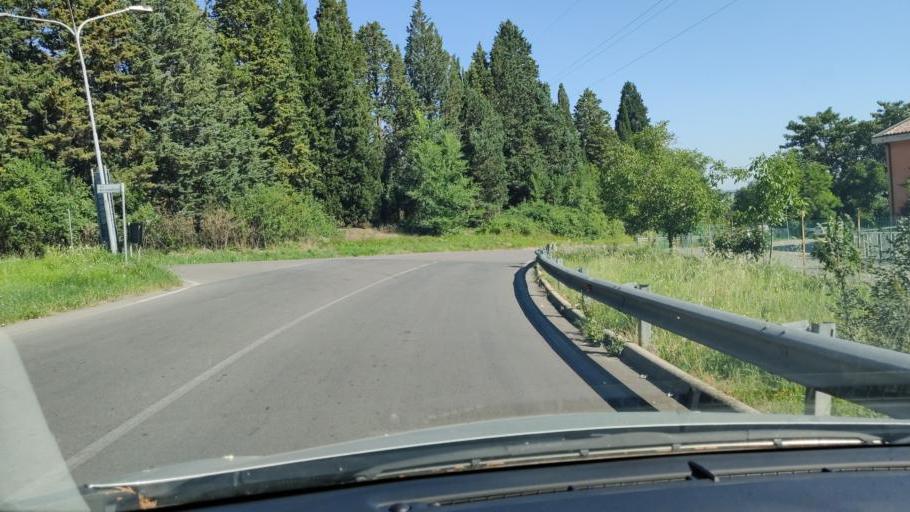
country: IT
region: Umbria
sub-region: Provincia di Perugia
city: Todi
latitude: 42.7791
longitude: 12.4195
